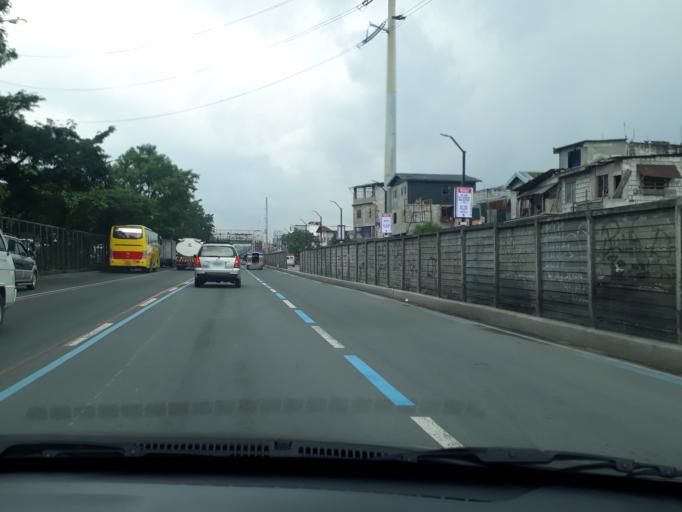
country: PH
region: Calabarzon
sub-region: Province of Rizal
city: Pateros
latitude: 14.5295
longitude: 121.0570
